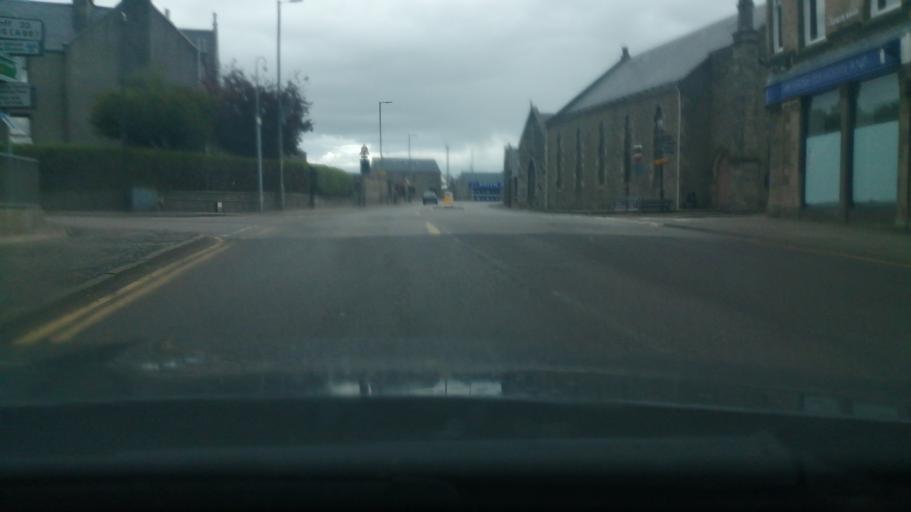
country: GB
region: Scotland
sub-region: Moray
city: Keith
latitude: 57.5432
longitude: -2.9500
